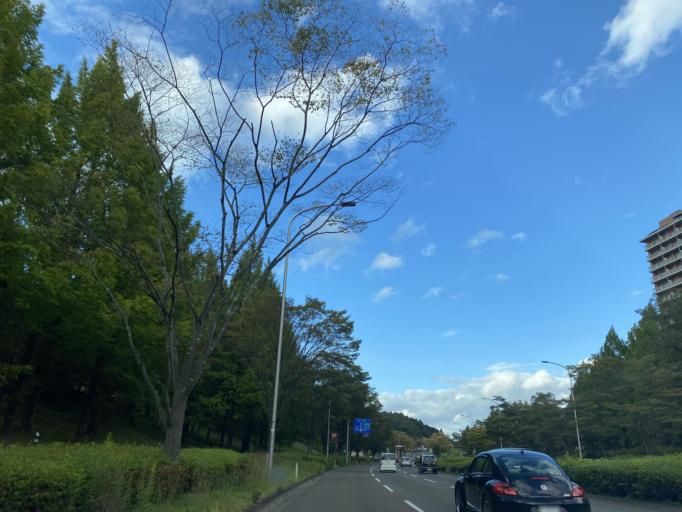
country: JP
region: Miyagi
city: Tomiya
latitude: 38.3413
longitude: 140.8387
